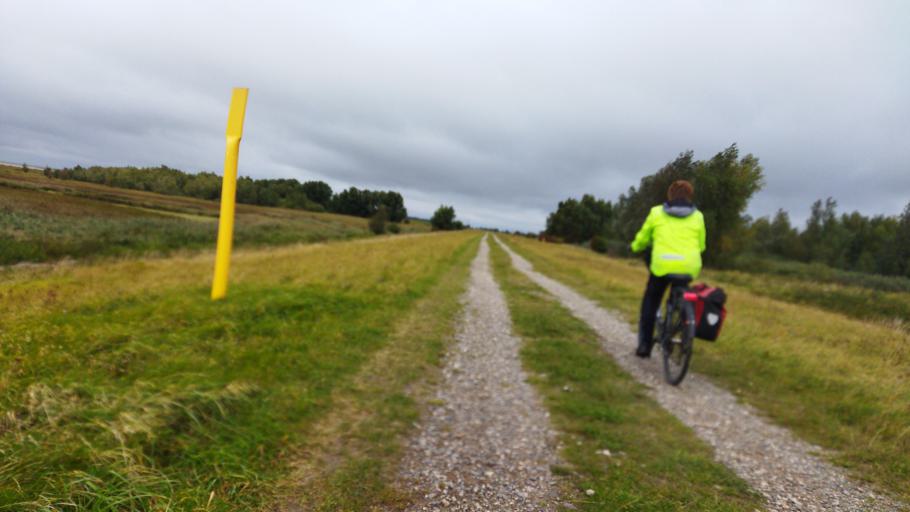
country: NL
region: Groningen
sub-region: Gemeente Delfzijl
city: Delfzijl
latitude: 53.3748
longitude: 7.0116
